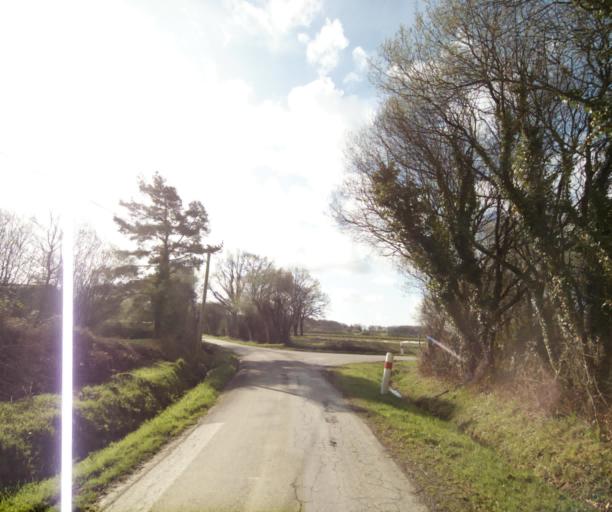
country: FR
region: Pays de la Loire
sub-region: Departement de la Loire-Atlantique
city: Bouvron
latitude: 47.4053
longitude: -1.8512
